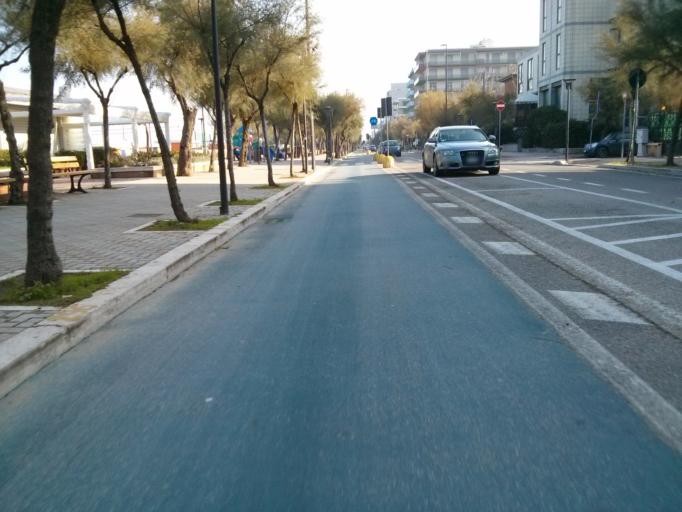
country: IT
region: The Marches
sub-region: Provincia di Pesaro e Urbino
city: Pesaro
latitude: 43.9185
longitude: 12.9114
